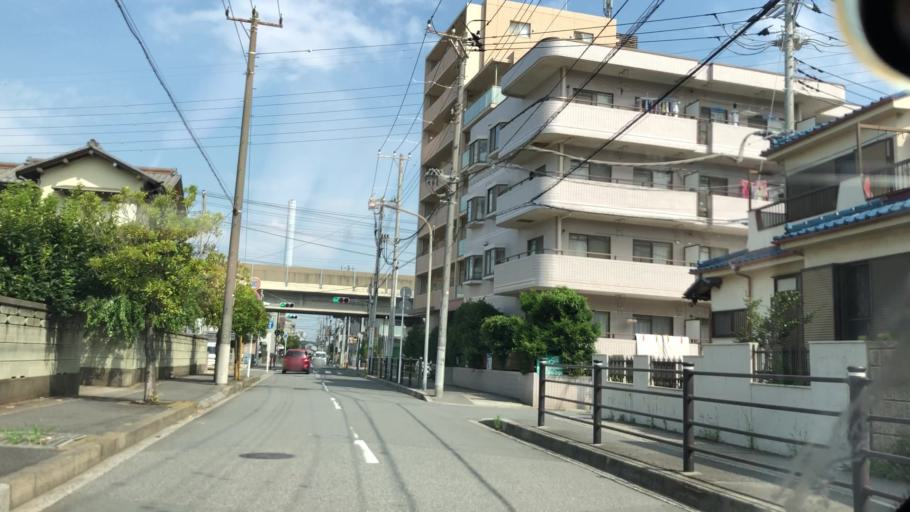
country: JP
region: Tokyo
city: Urayasu
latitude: 35.6787
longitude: 139.9108
